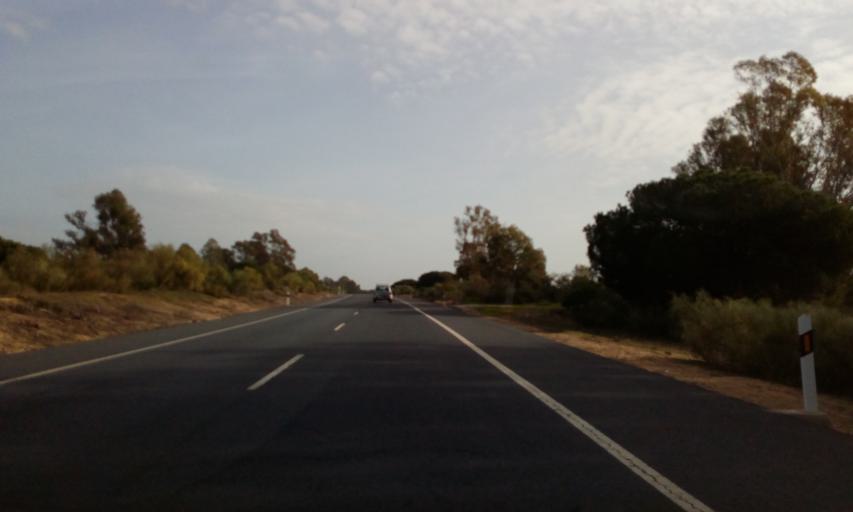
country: ES
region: Andalusia
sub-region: Provincia de Huelva
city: Palos de la Frontera
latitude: 37.1599
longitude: -6.8815
